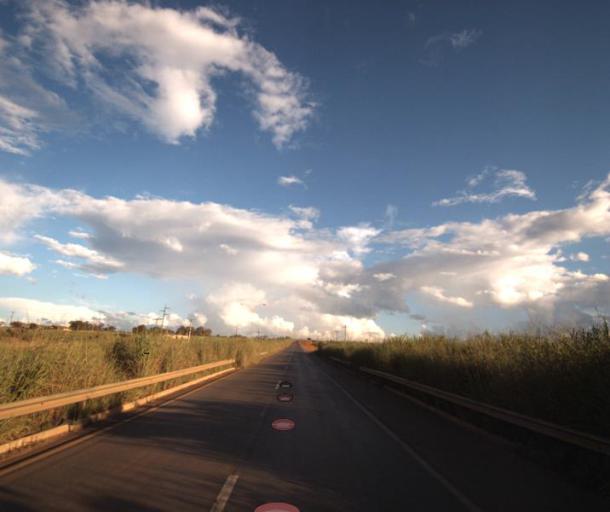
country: BR
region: Goias
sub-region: Anapolis
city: Anapolis
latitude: -16.3085
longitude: -48.9235
